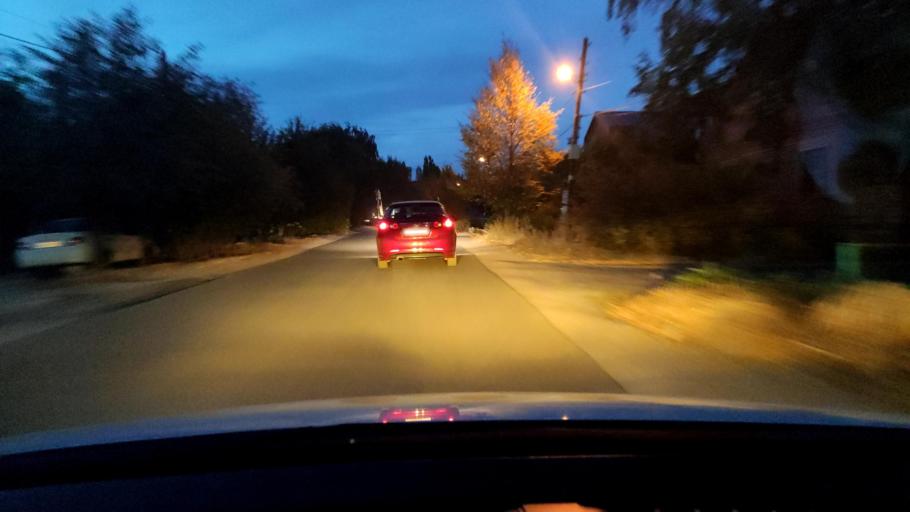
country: RU
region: Voronezj
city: Voronezh
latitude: 51.6996
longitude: 39.1687
